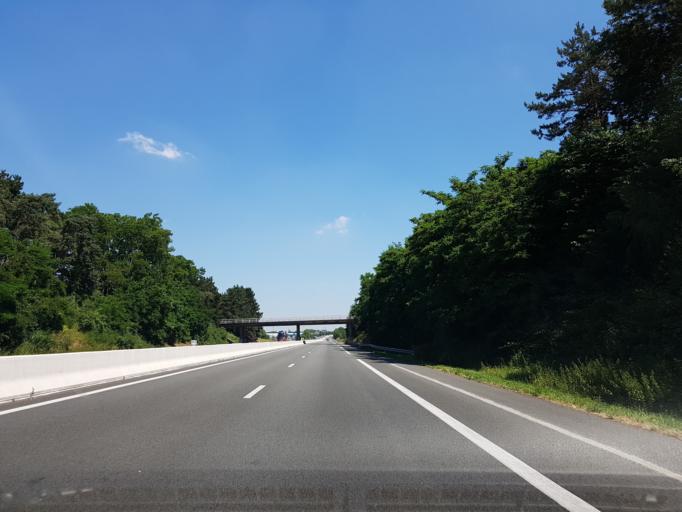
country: FR
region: Nord-Pas-de-Calais
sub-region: Departement du Nord
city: Raillencourt-Sainte-Olle
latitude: 50.1768
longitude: 3.1846
